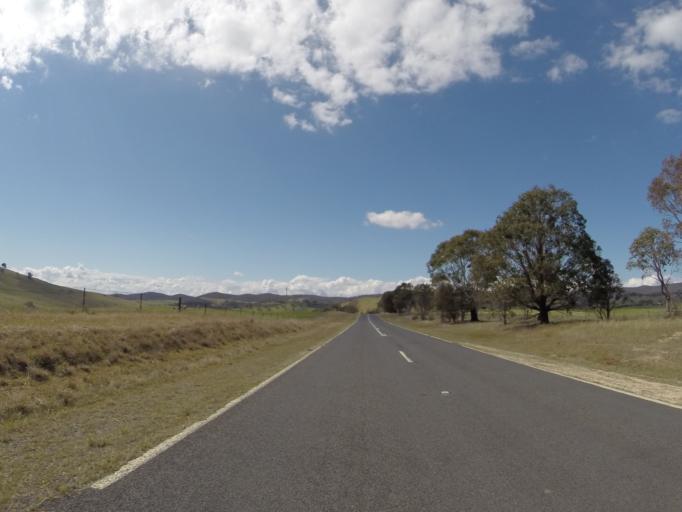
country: AU
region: Australian Capital Territory
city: Macarthur
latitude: -35.4076
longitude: 148.9517
